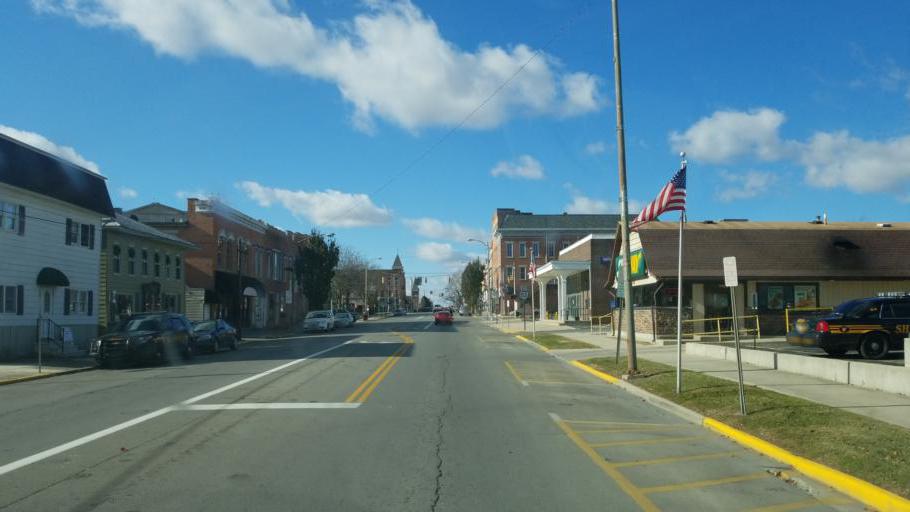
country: US
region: Ohio
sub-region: Hardin County
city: Kenton
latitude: 40.6482
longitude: -83.6068
